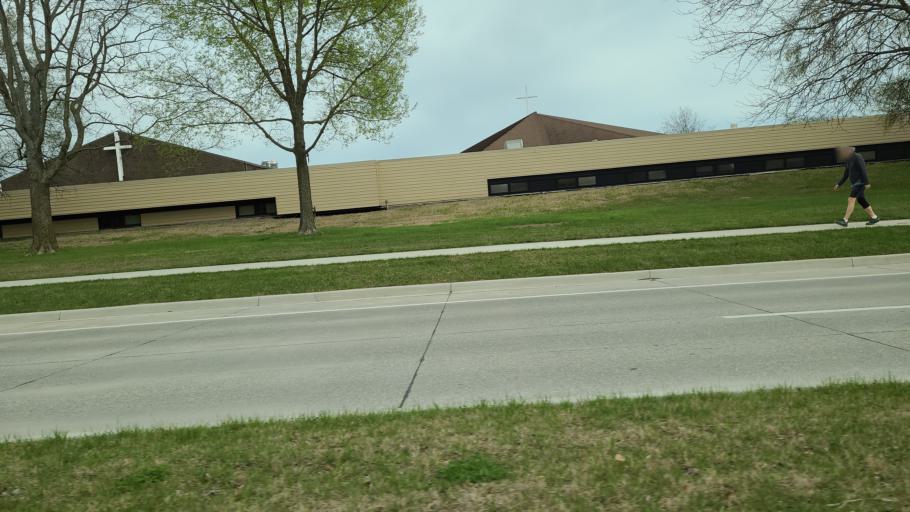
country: US
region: Kansas
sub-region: Douglas County
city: Lawrence
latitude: 38.9601
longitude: -95.2790
